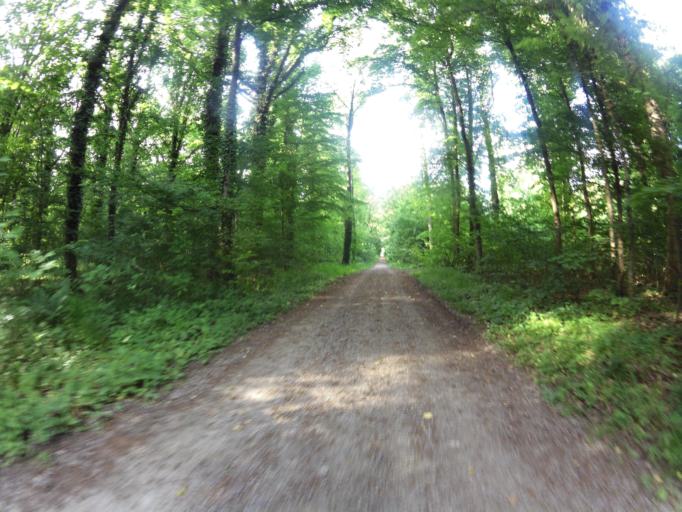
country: DE
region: Bavaria
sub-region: Regierungsbezirk Unterfranken
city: Frickenhausen
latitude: 49.6900
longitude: 10.0727
